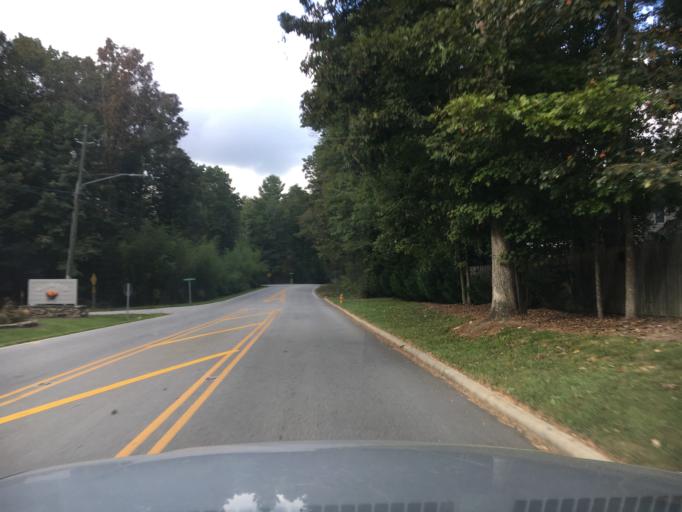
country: US
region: North Carolina
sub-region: Henderson County
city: Fletcher
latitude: 35.4337
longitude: -82.5208
